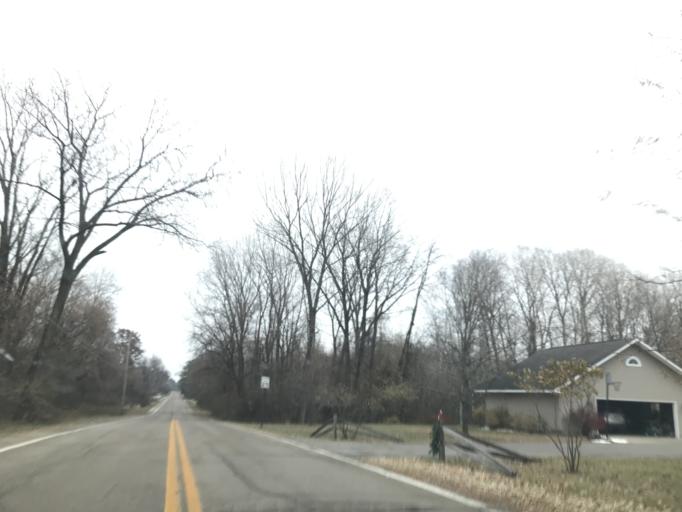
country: US
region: Wisconsin
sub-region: Marinette County
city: Marinette
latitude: 45.0780
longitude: -87.6294
